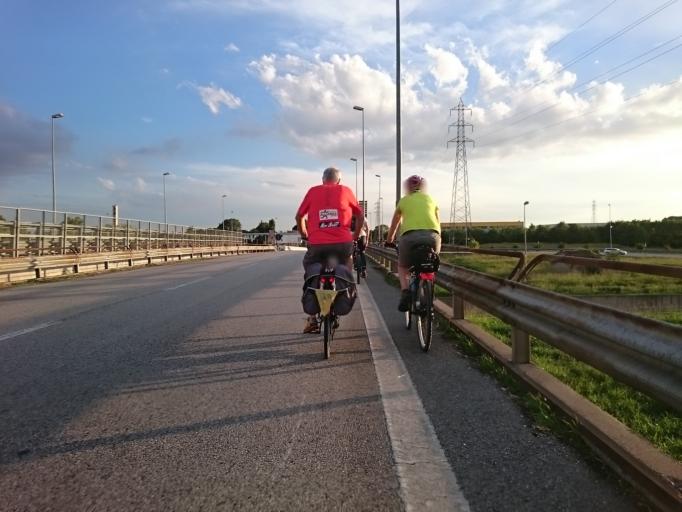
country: IT
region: Veneto
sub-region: Provincia di Padova
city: Ponte San Nicolo
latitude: 45.3823
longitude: 11.9392
